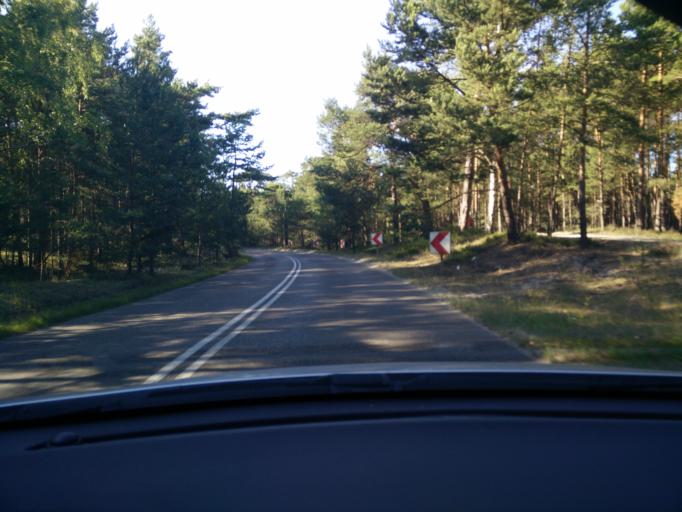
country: PL
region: Pomeranian Voivodeship
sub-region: Powiat pucki
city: Hel
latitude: 54.6257
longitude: 18.7946
